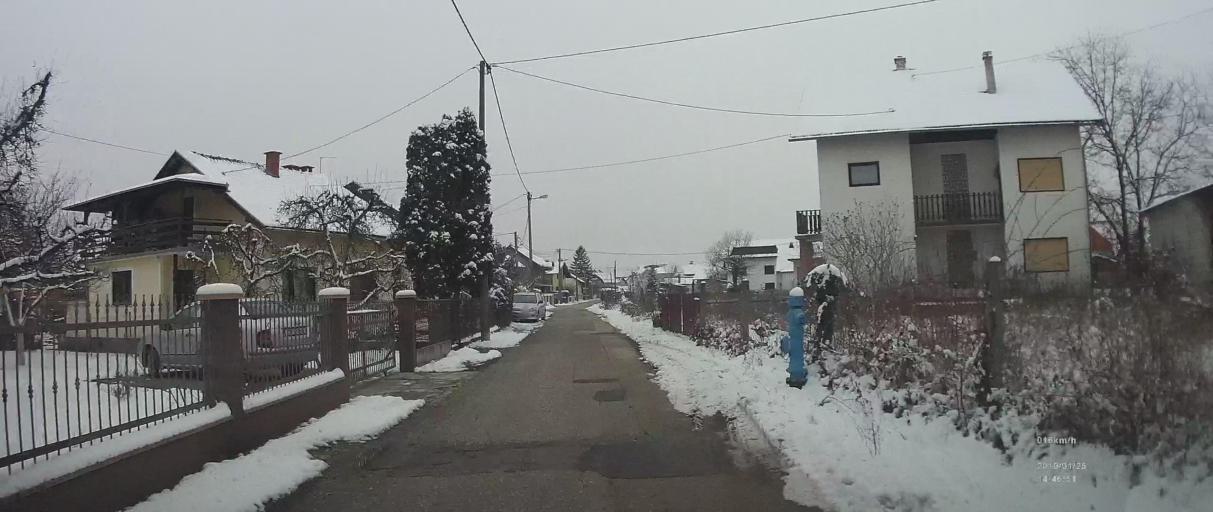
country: HR
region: Zagrebacka
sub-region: Grad Velika Gorica
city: Velika Gorica
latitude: 45.7031
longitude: 16.0776
